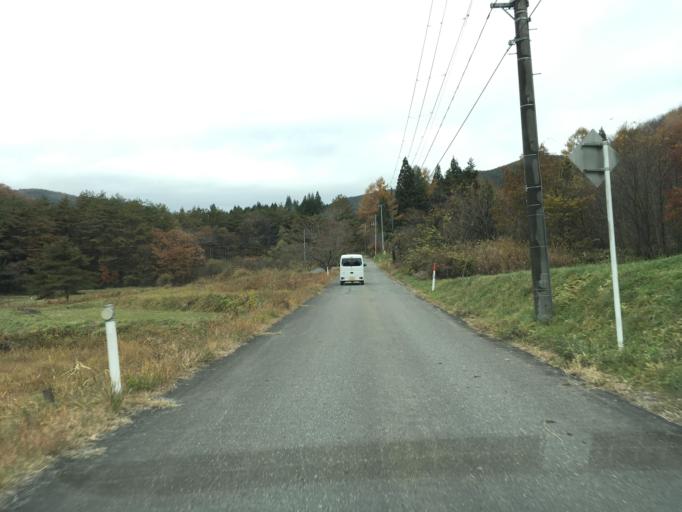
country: JP
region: Iwate
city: Mizusawa
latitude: 39.1160
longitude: 141.3256
